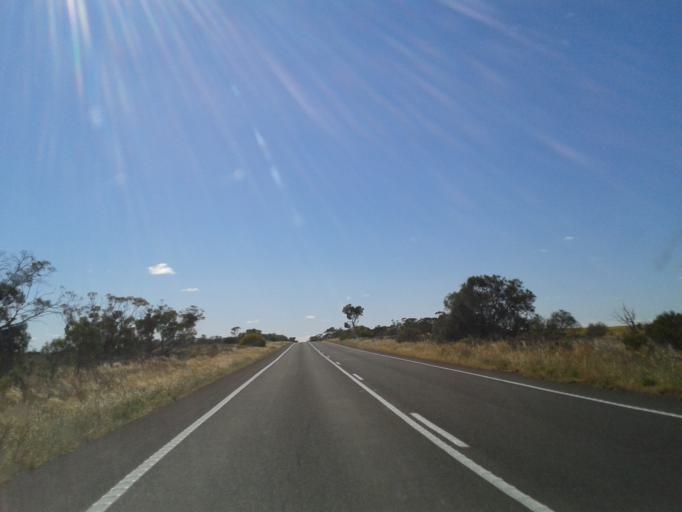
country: AU
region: South Australia
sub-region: Renmark Paringa
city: Renmark
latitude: -34.2745
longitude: 141.2167
